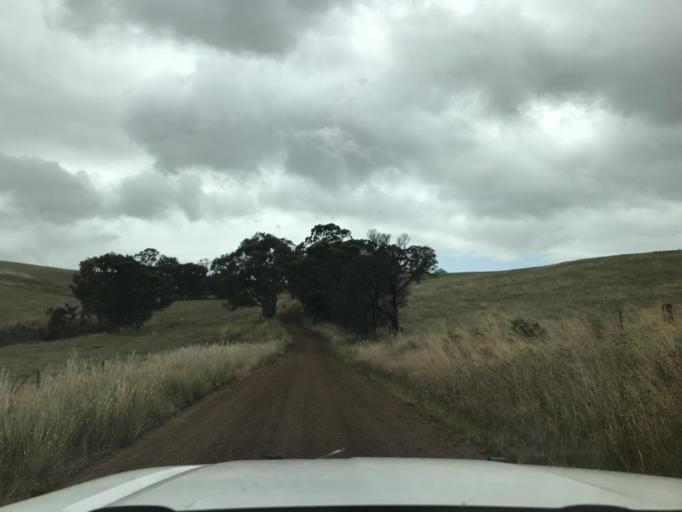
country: AU
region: South Australia
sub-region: Wattle Range
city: Penola
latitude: -37.2345
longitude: 141.4639
